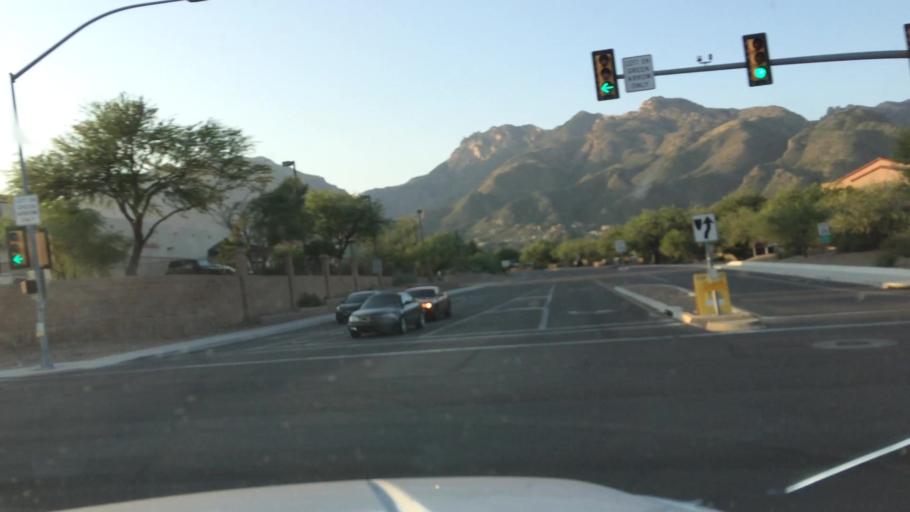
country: US
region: Arizona
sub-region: Pima County
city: Catalina Foothills
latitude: 32.3088
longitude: -110.8444
